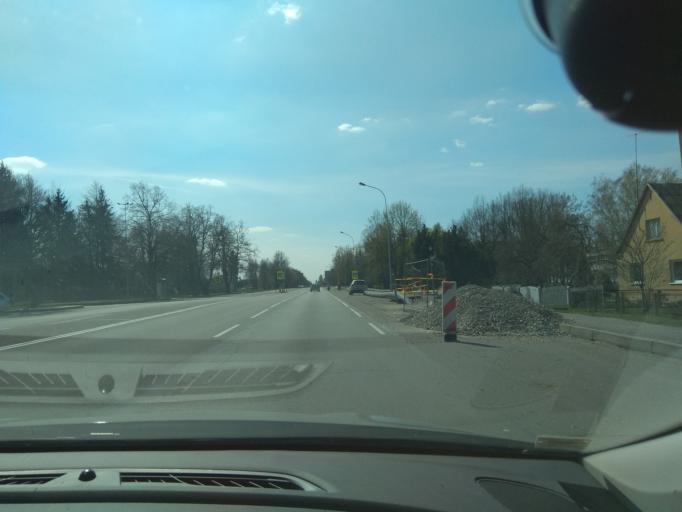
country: LT
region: Marijampoles apskritis
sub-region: Marijampole Municipality
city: Marijampole
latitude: 54.5742
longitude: 23.3679
